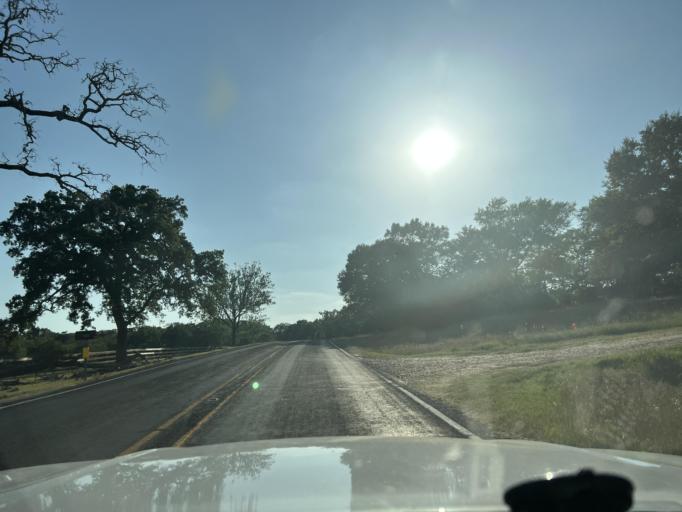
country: US
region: Texas
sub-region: Washington County
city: Brenham
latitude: 30.2343
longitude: -96.2750
